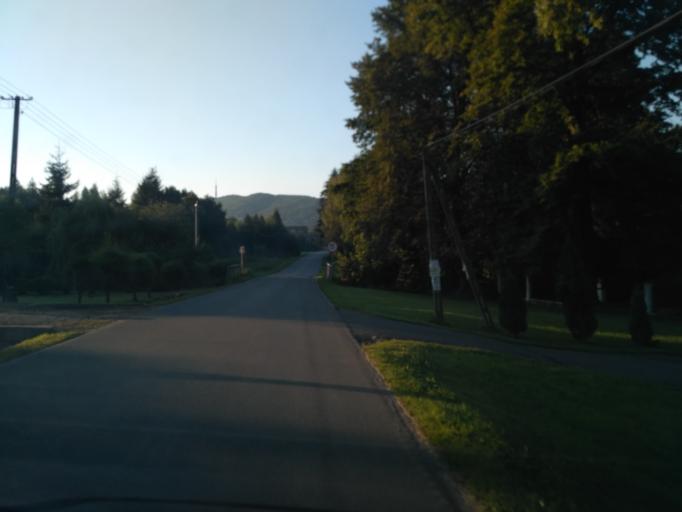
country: PL
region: Subcarpathian Voivodeship
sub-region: Powiat krosnienski
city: Odrzykon
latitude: 49.7753
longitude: 21.7792
